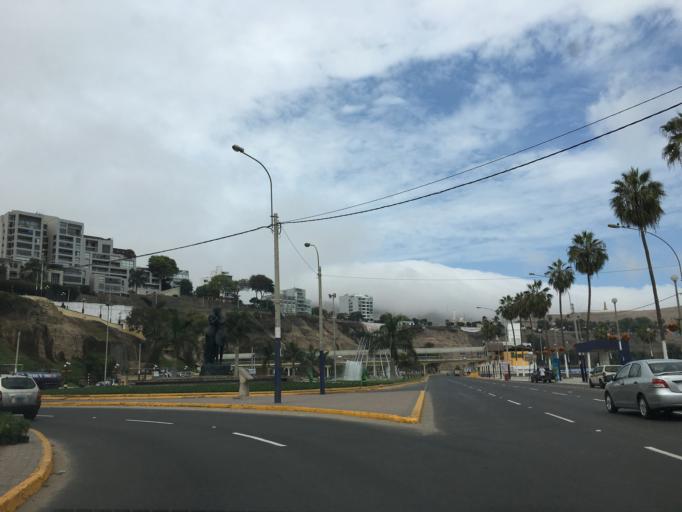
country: PE
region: Lima
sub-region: Lima
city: Surco
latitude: -12.1618
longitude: -77.0259
